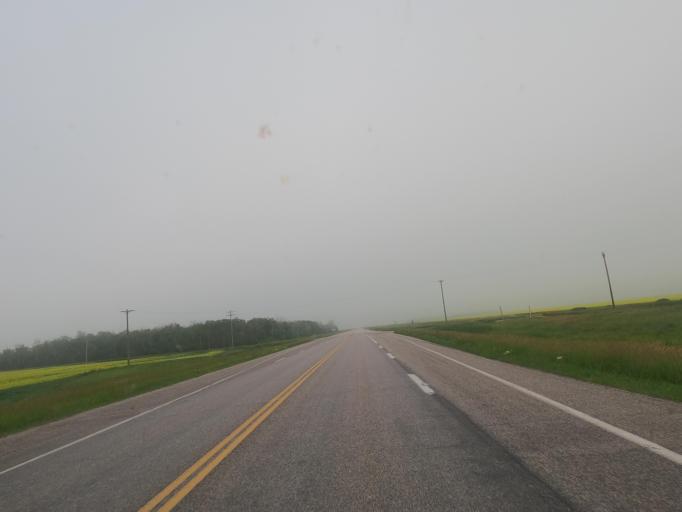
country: CA
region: Manitoba
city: Carman
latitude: 49.7128
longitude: -97.9132
